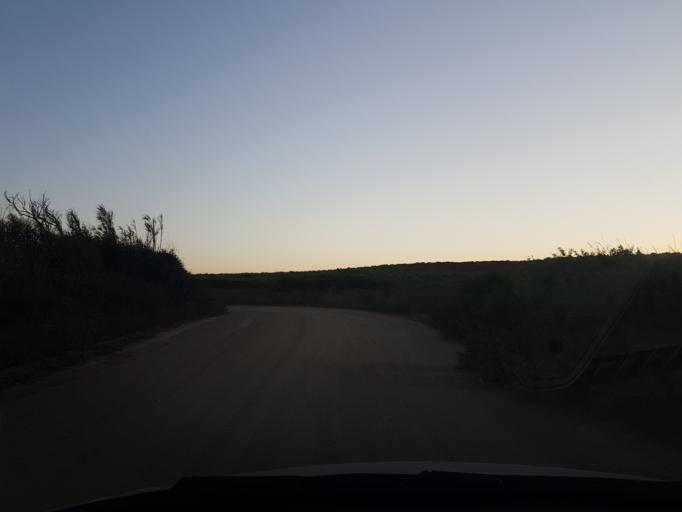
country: IT
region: Sardinia
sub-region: Provincia di Oristano
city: Riola Sardo
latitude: 40.0417
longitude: 8.3968
